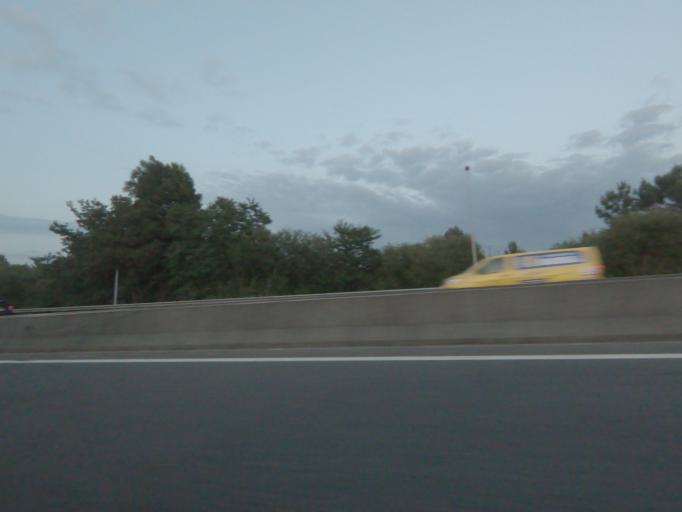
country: ES
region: Galicia
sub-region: Provincia de Pontevedra
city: Tui
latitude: 42.0848
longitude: -8.6272
